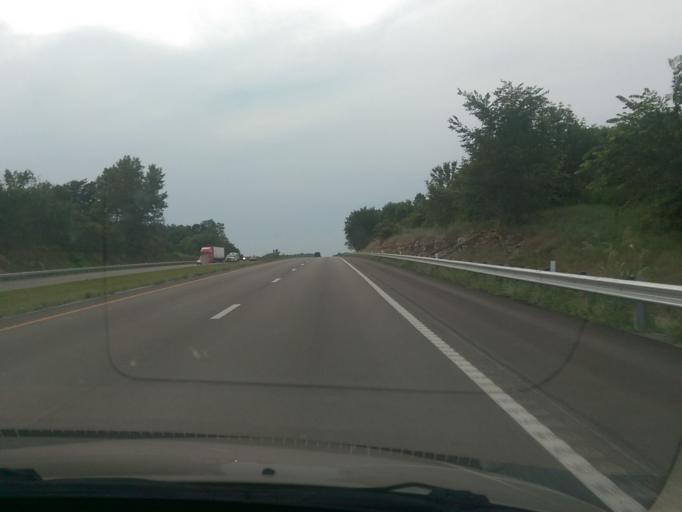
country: US
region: Missouri
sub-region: Andrew County
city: Savannah
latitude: 39.9291
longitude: -94.9216
